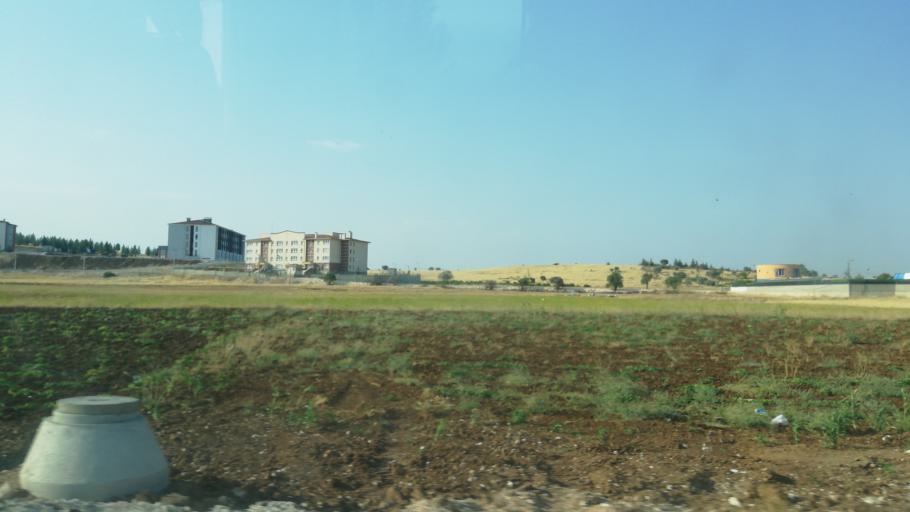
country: TR
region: Mardin
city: Acirli
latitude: 37.4373
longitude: 41.3089
